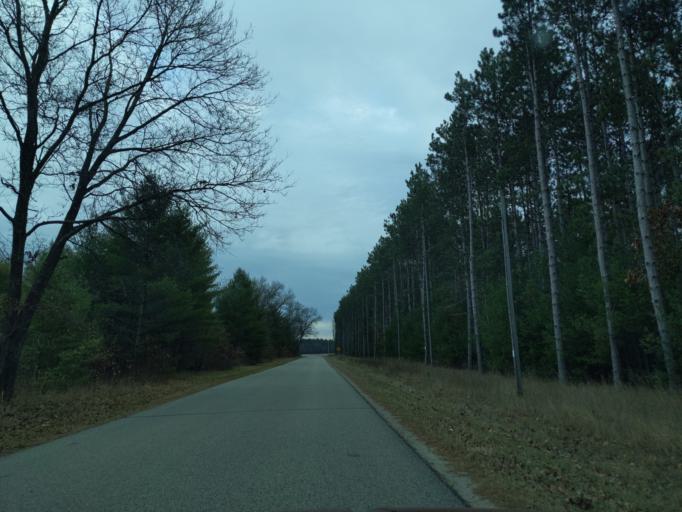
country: US
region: Wisconsin
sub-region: Waushara County
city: Wautoma
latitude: 44.0457
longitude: -89.2902
